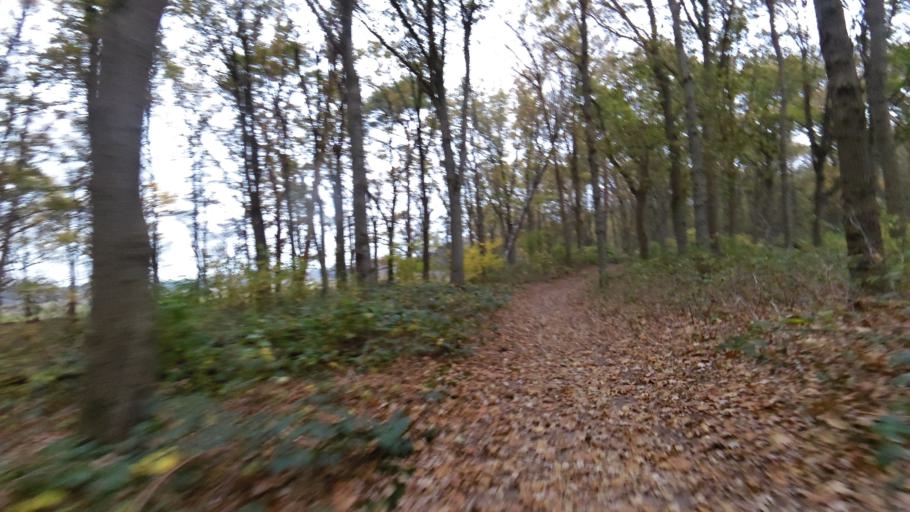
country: NL
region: North Holland
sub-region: Gemeente Laren
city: Laren
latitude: 52.2223
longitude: 5.2179
